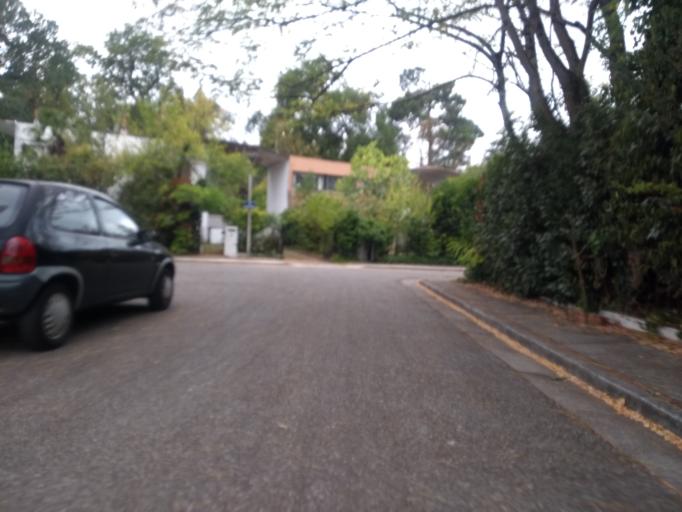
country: FR
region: Aquitaine
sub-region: Departement de la Gironde
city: Pessac
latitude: 44.7983
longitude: -0.6485
